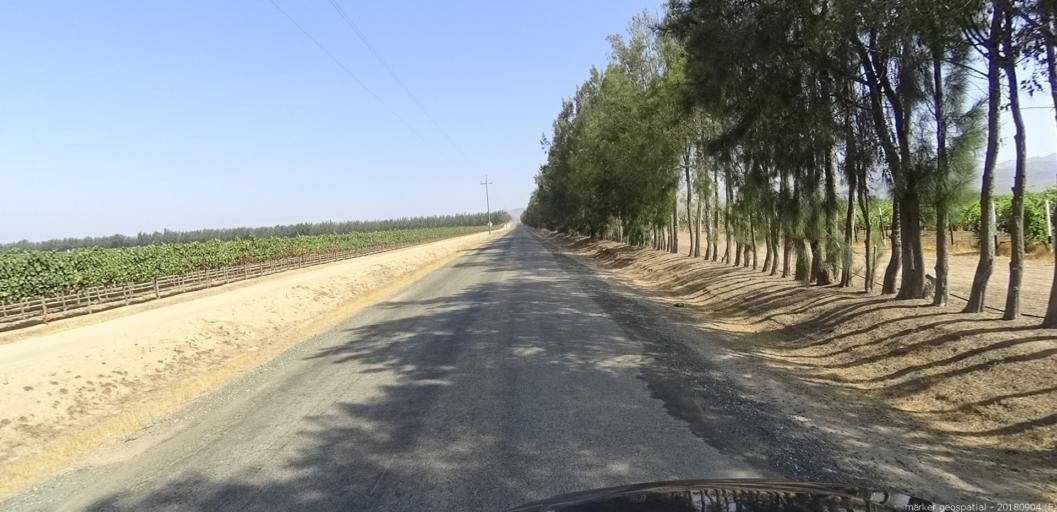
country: US
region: California
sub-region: Monterey County
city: Soledad
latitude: 36.4896
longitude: -121.3648
